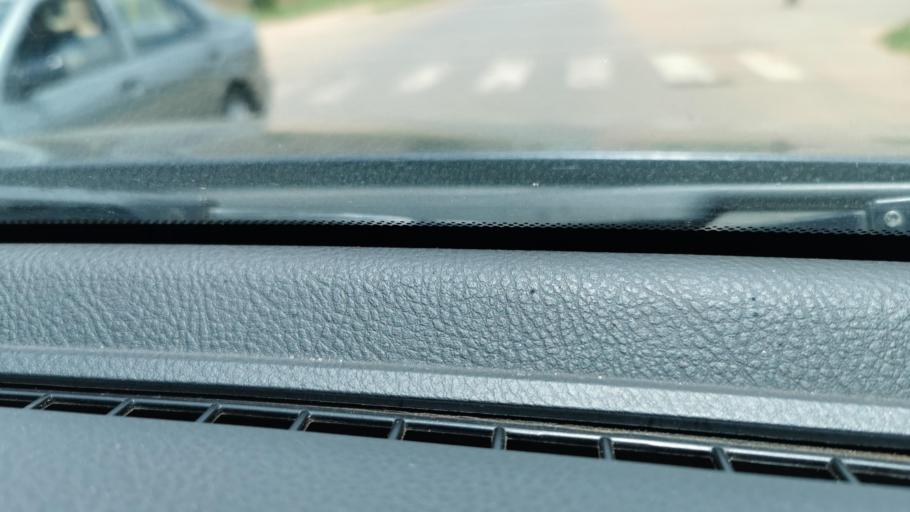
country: TG
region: Maritime
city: Lome
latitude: 6.2111
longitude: 1.1962
